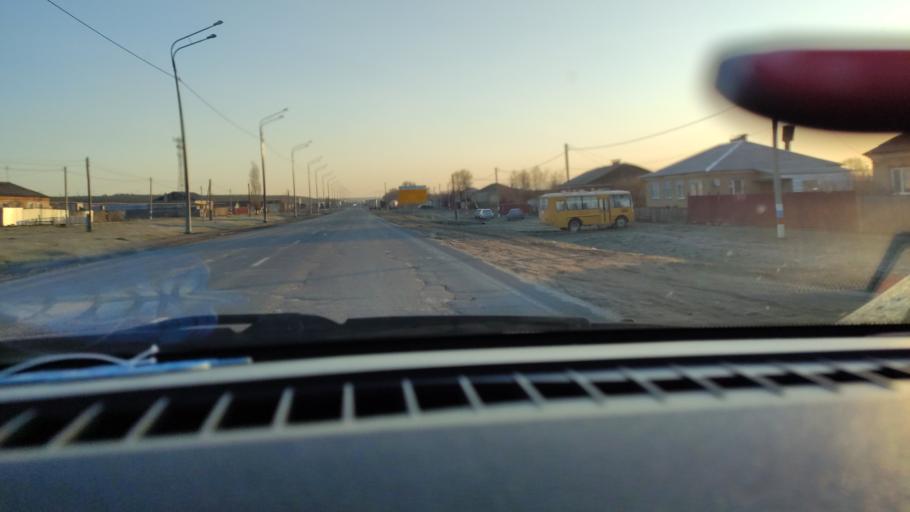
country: RU
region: Saratov
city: Sinodskoye
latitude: 51.9946
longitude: 46.6720
